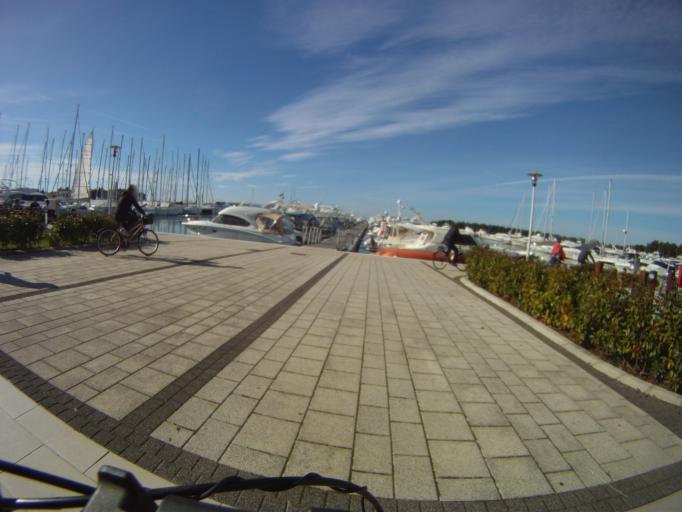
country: HR
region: Istarska
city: Novigrad
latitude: 45.3204
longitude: 13.5635
